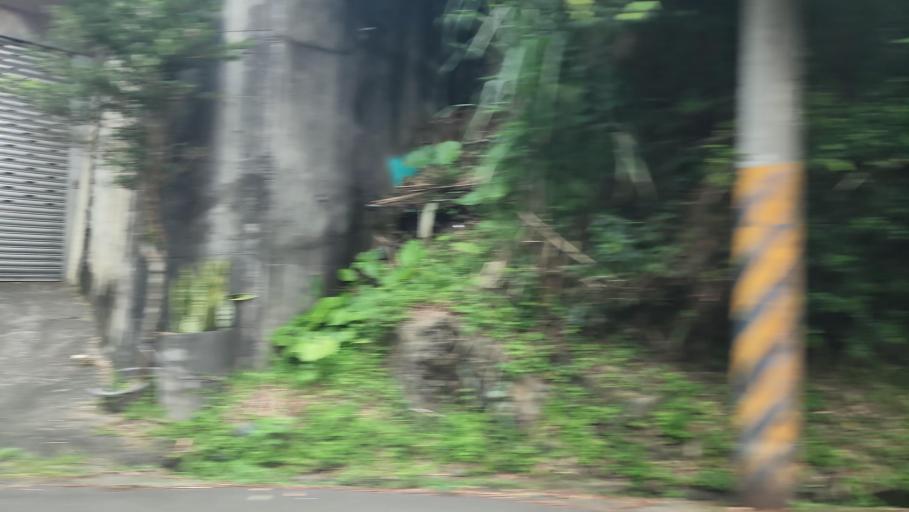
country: TW
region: Taiwan
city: Daxi
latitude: 24.8747
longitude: 121.4141
